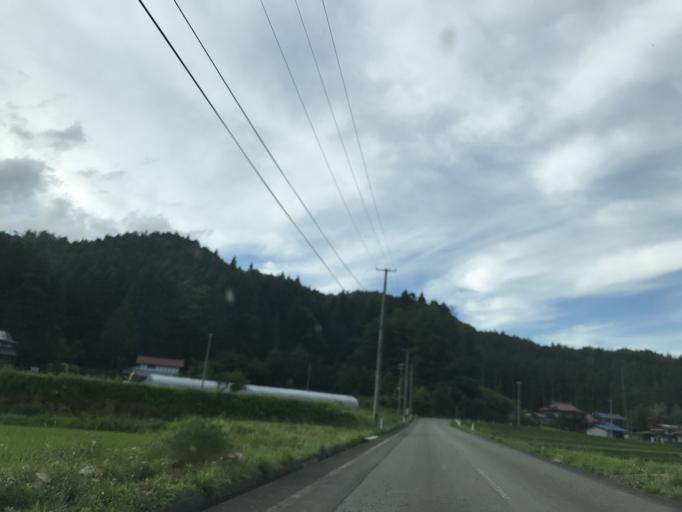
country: JP
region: Iwate
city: Ichinoseki
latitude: 38.9002
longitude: 140.9791
